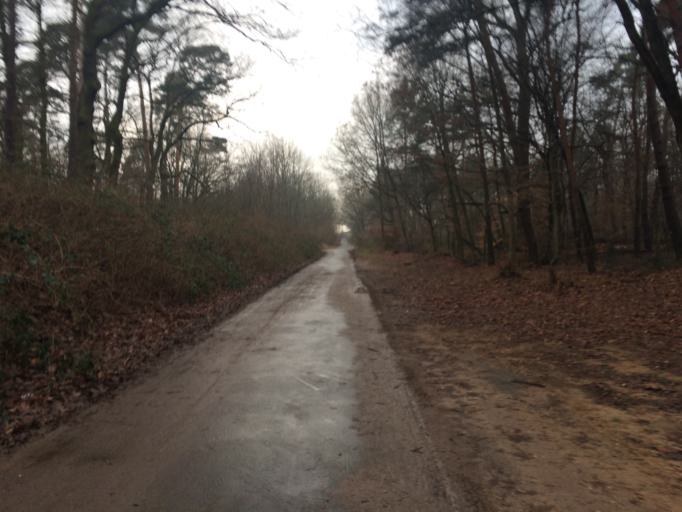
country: DE
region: Hesse
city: Morfelden-Walldorf
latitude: 50.0382
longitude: 8.6009
